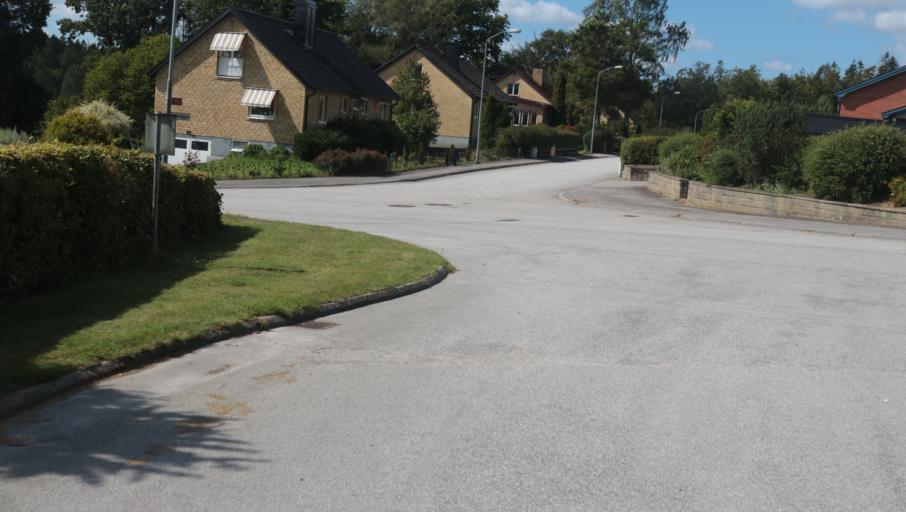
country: SE
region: Blekinge
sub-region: Karlshamns Kommun
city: Svangsta
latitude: 56.2580
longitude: 14.7672
